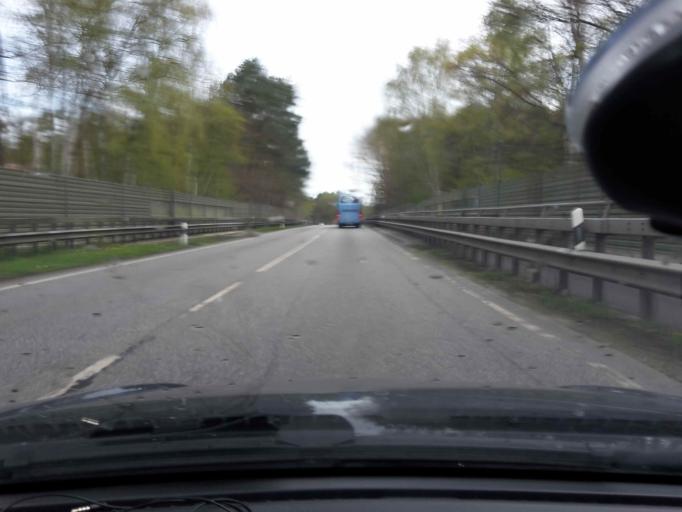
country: DE
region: Lower Saxony
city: Buxtehude
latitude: 53.4679
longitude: 9.6746
